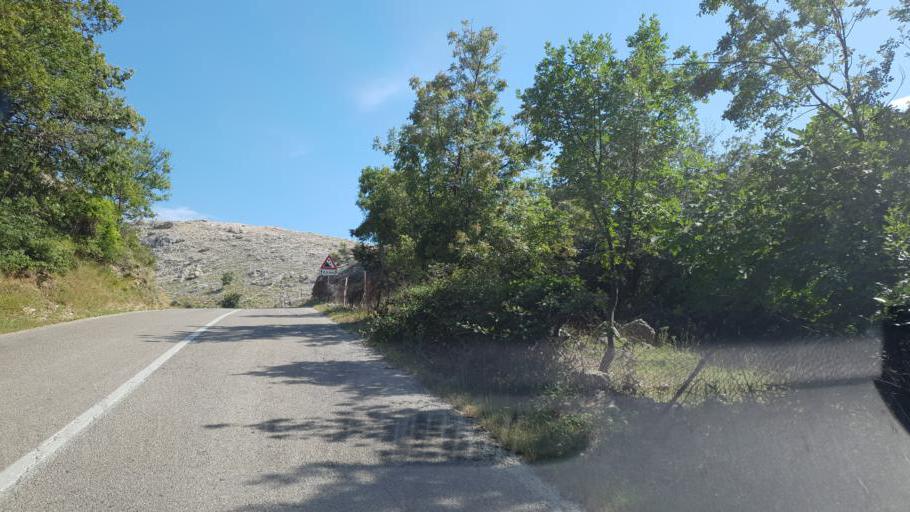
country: HR
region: Primorsko-Goranska
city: Punat
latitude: 44.9786
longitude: 14.6590
